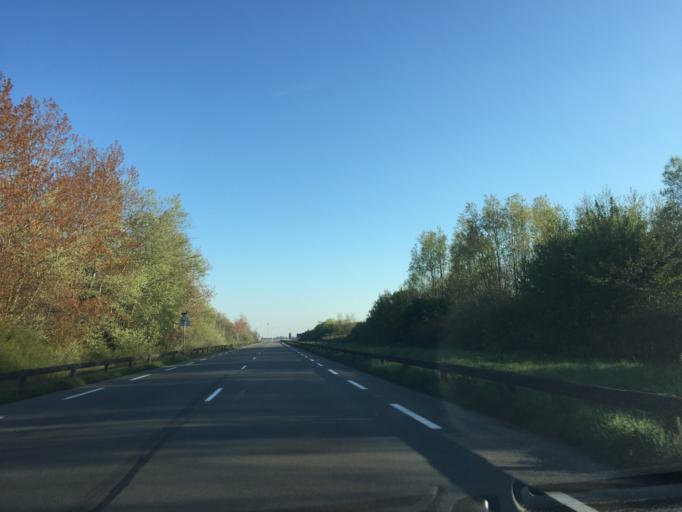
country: FR
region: Nord-Pas-de-Calais
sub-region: Departement du Nord
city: Loon-Plage
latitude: 51.0071
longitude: 2.1972
